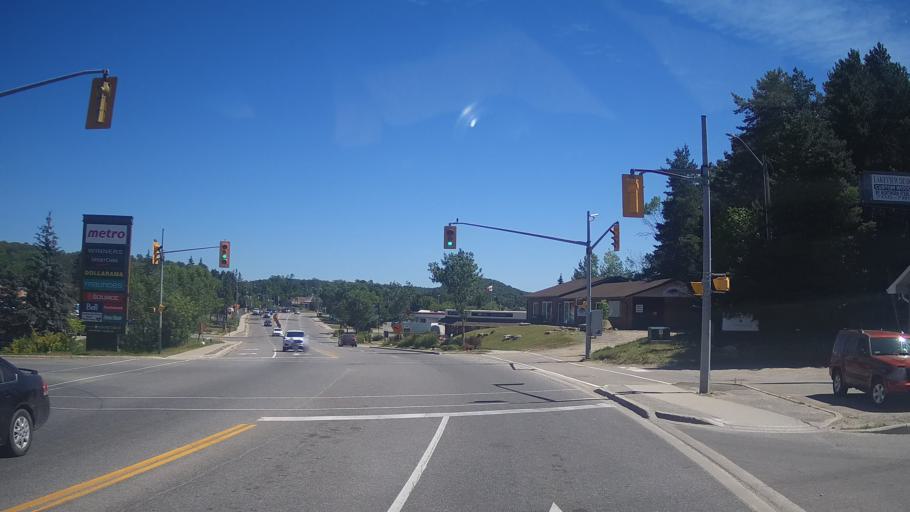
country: CA
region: Ontario
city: Huntsville
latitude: 45.3330
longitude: -79.2066
